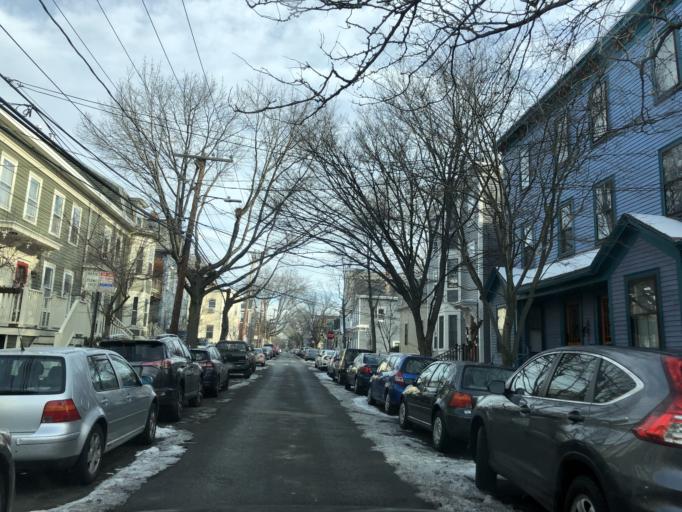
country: US
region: Massachusetts
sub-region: Middlesex County
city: Cambridge
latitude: 42.3613
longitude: -71.1114
